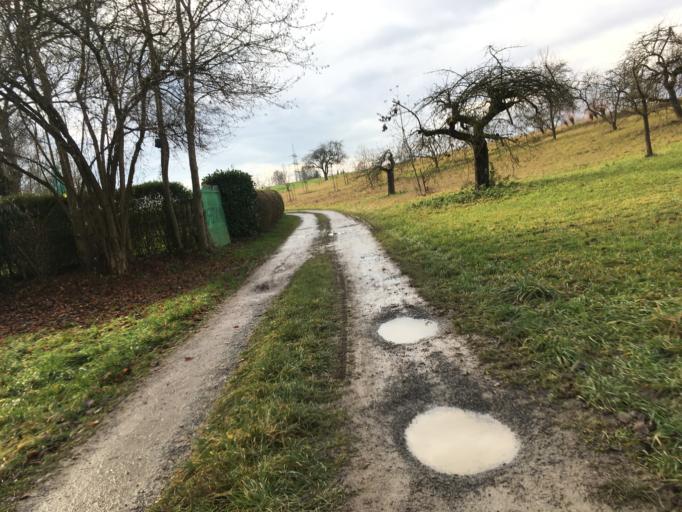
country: DE
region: Baden-Wuerttemberg
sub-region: Regierungsbezirk Stuttgart
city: Talheim
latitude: 49.1076
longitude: 9.1768
